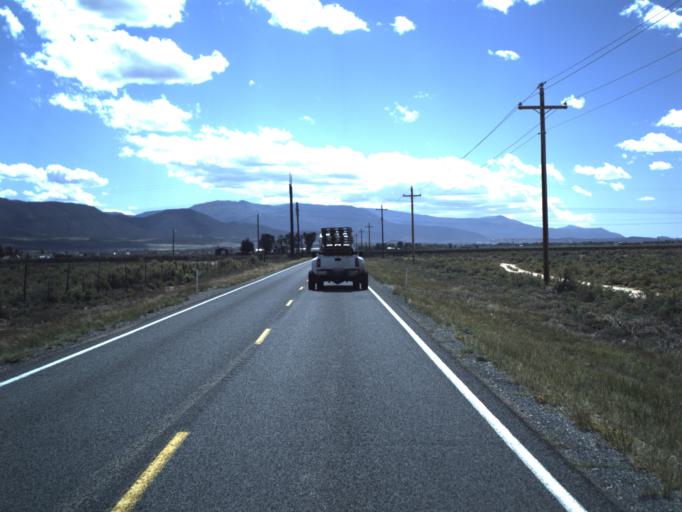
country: US
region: Utah
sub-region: Iron County
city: Enoch
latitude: 37.8053
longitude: -113.0506
